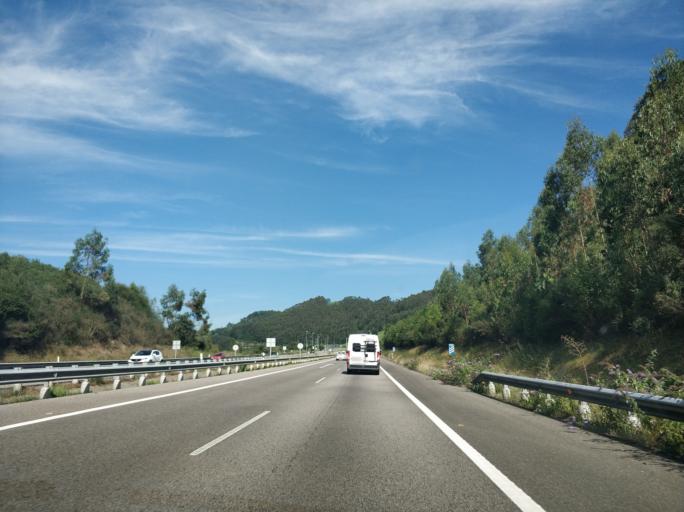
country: ES
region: Asturias
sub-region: Province of Asturias
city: Soto del Barco
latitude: 43.5191
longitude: -6.0736
